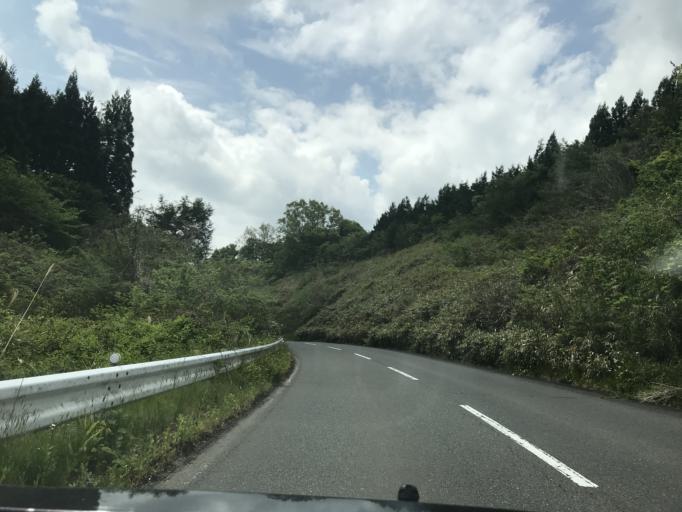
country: JP
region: Miyagi
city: Furukawa
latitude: 38.7190
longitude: 140.9198
